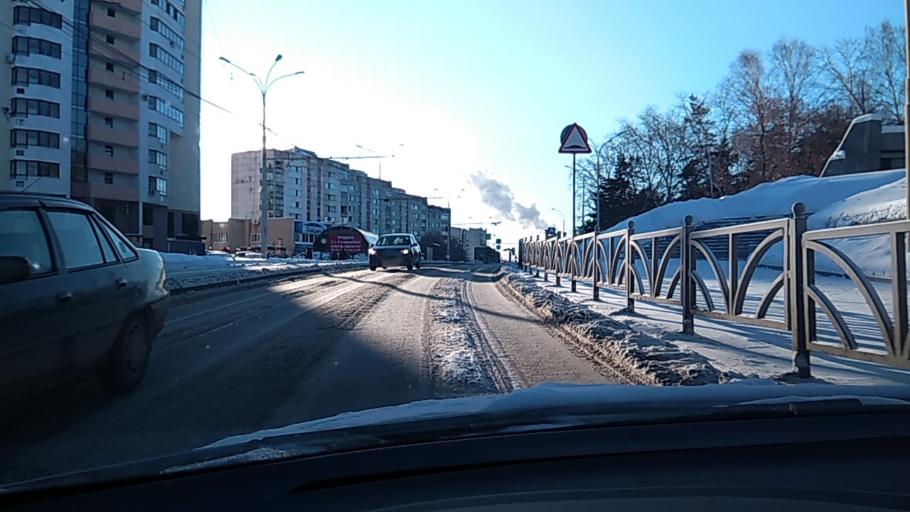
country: RU
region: Sverdlovsk
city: Yekaterinburg
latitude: 56.8277
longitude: 60.5805
